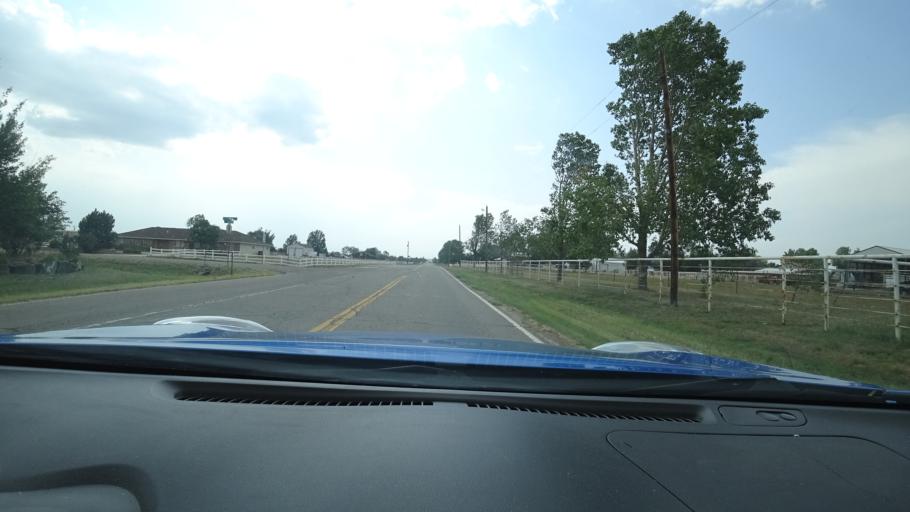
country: US
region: Colorado
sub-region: Adams County
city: Brighton
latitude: 39.9217
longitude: -104.8354
